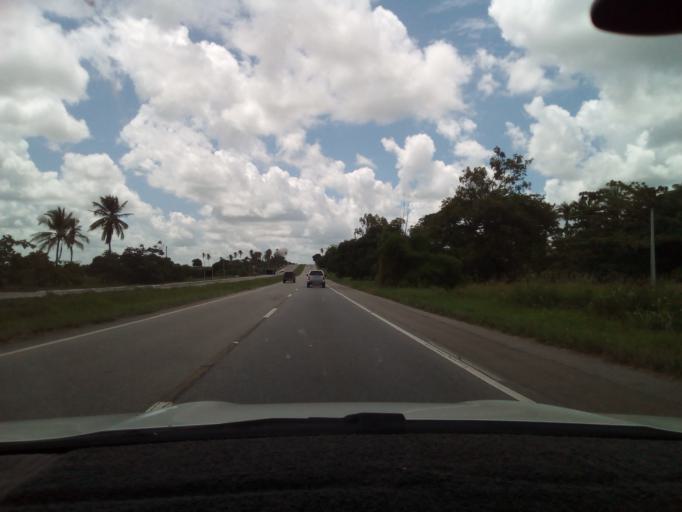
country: BR
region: Paraiba
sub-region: Pilar
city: Pilar
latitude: -7.1905
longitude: -35.2464
